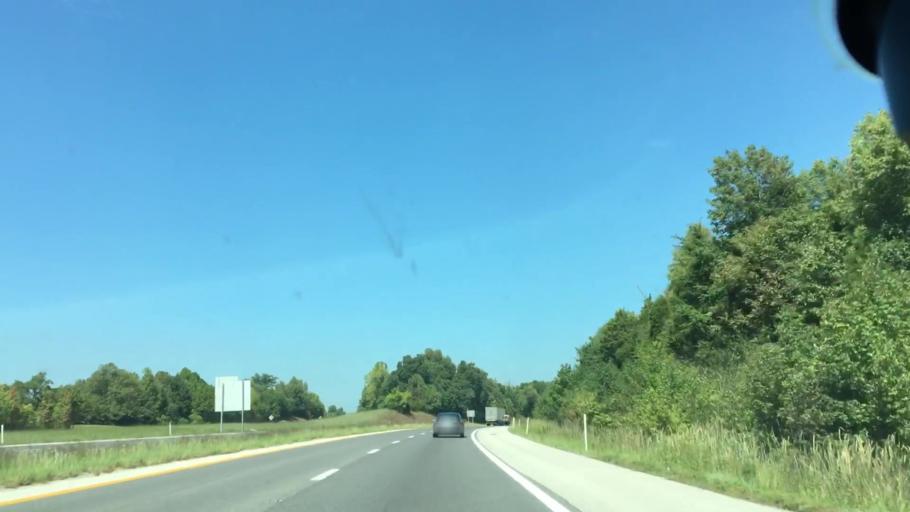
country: US
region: Kentucky
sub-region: Hopkins County
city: Madisonville
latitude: 37.3616
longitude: -87.4897
